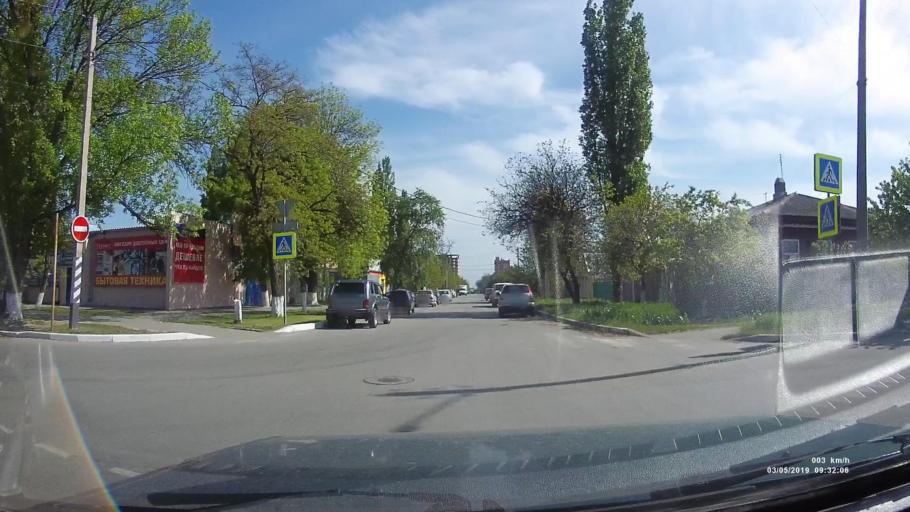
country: RU
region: Rostov
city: Azov
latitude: 47.1010
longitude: 39.4284
